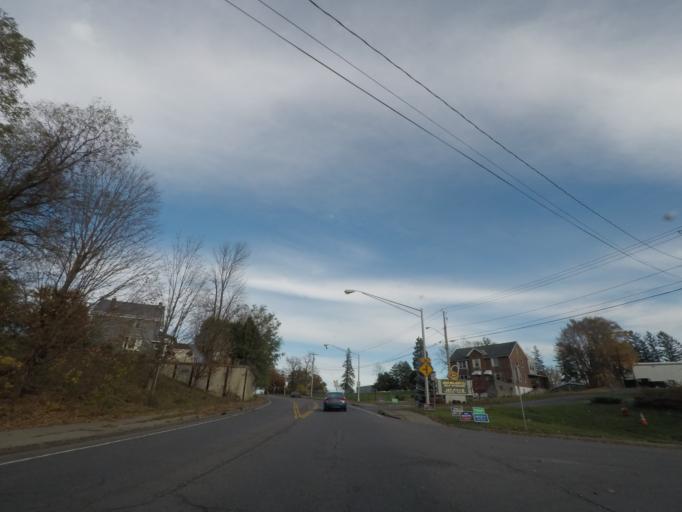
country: US
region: New York
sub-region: Albany County
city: Delmar
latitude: 42.6343
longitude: -73.7962
